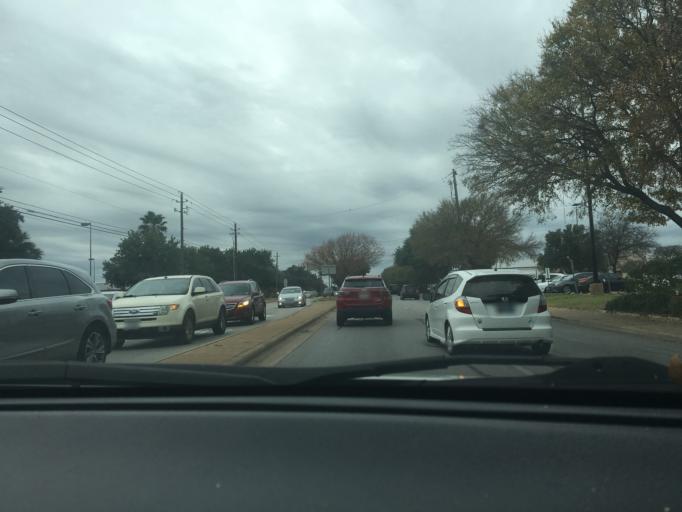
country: US
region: Texas
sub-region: Travis County
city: Rollingwood
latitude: 30.2294
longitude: -97.8205
